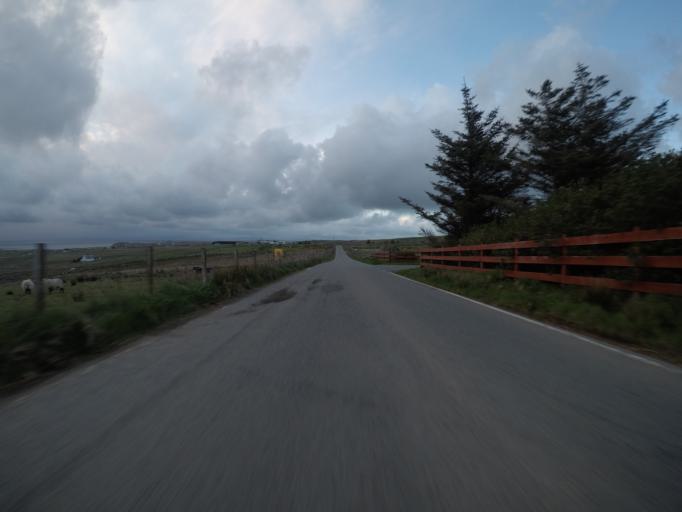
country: GB
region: Scotland
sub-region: Highland
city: Portree
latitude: 57.6396
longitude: -6.3765
